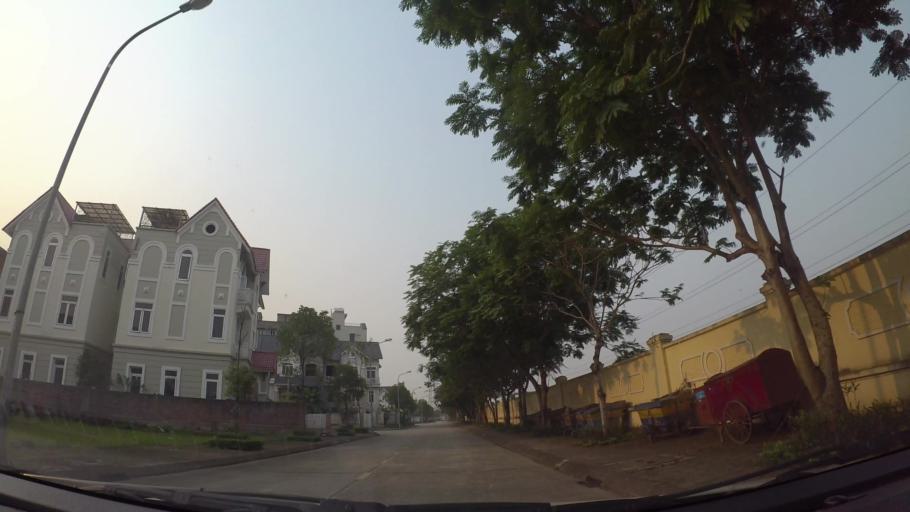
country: VN
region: Ha Noi
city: Cau Dien
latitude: 21.0052
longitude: 105.7343
